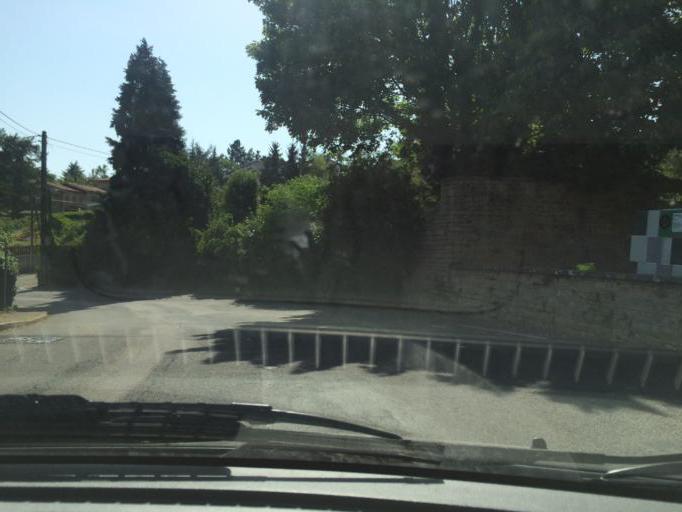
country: FR
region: Rhone-Alpes
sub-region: Departement du Rhone
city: Limonest
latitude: 45.8256
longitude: 4.7946
